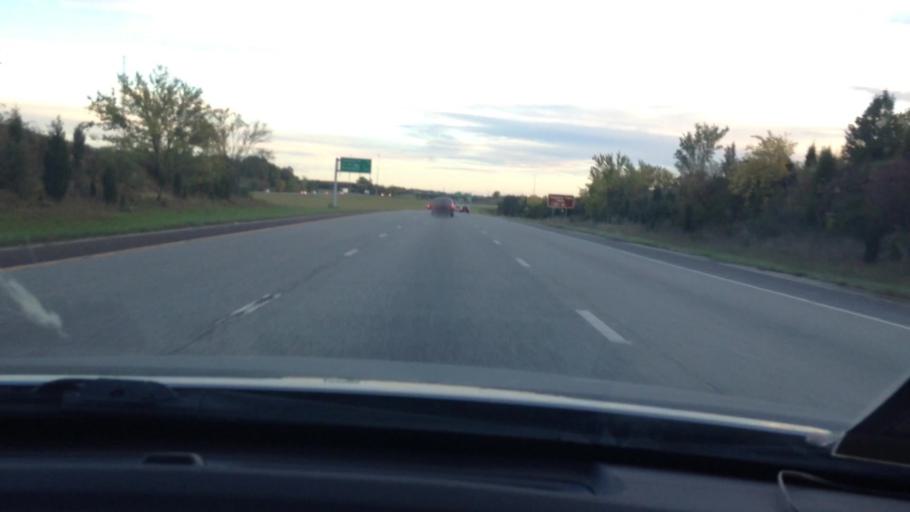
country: US
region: Kansas
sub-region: Wyandotte County
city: Edwardsville
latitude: 39.0318
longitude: -94.7882
